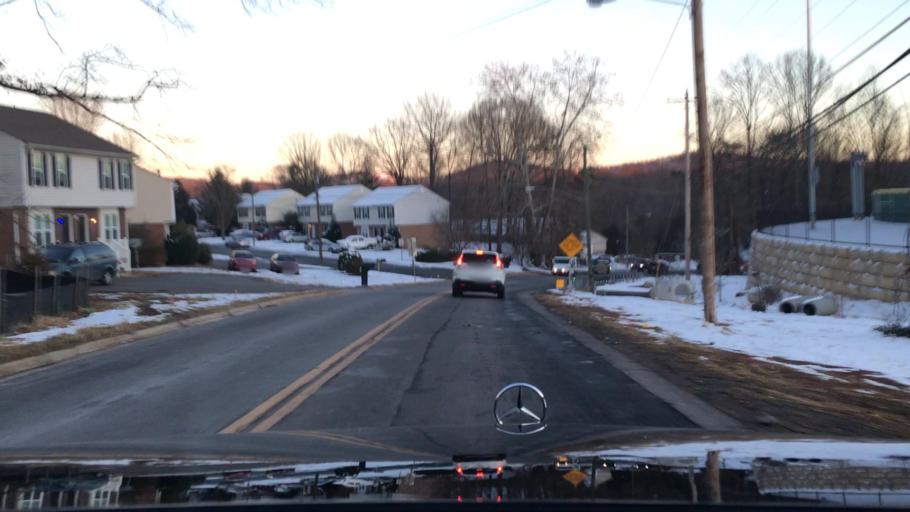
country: US
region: Virginia
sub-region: City of Lynchburg
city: West Lynchburg
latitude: 37.3624
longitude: -79.2029
